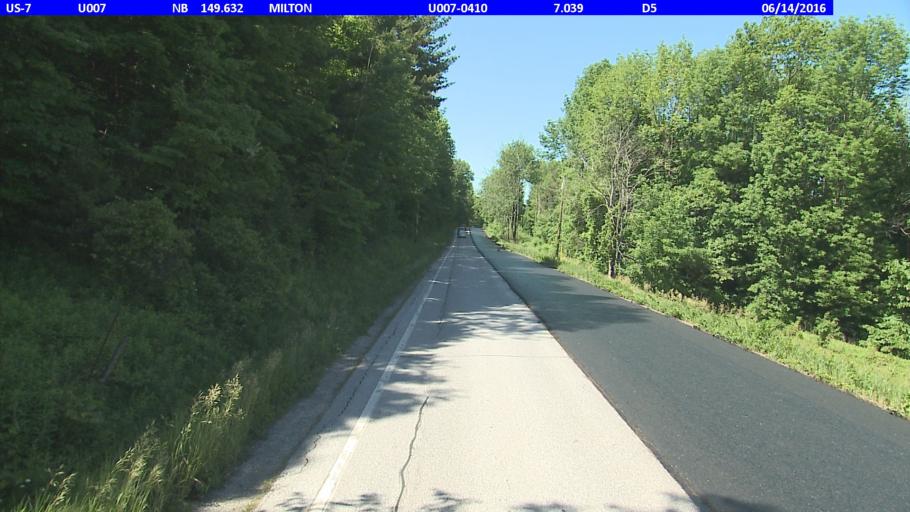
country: US
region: Vermont
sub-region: Chittenden County
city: Milton
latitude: 44.6679
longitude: -73.1115
